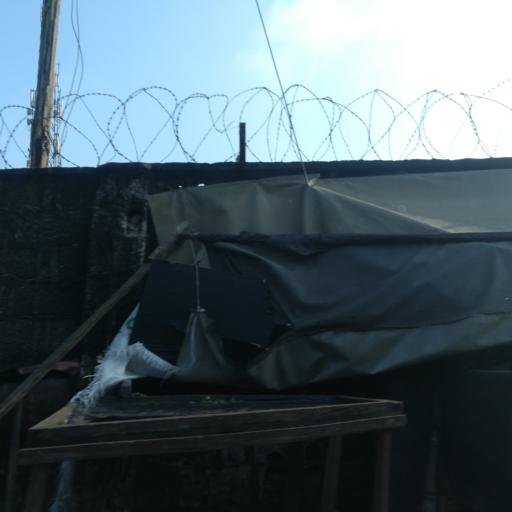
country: NG
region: Rivers
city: Port Harcourt
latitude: 4.8579
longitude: 6.9656
